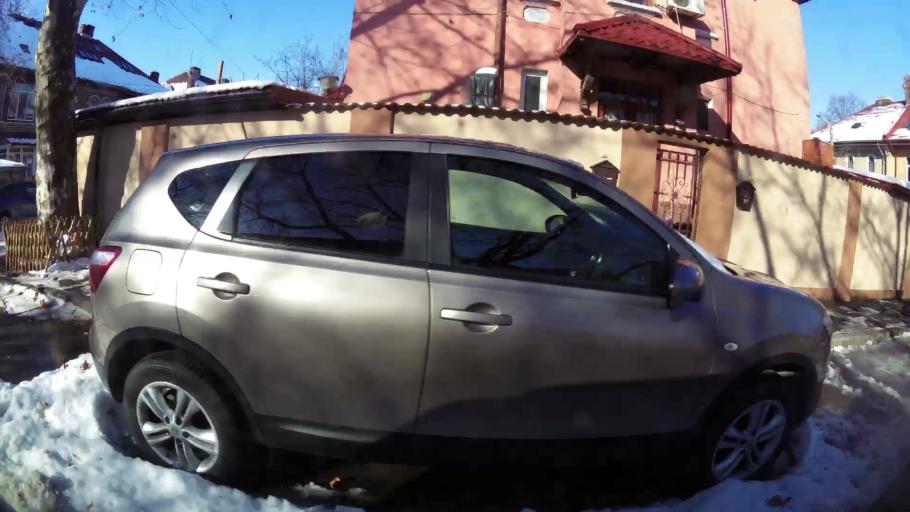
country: RO
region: Bucuresti
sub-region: Municipiul Bucuresti
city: Bucuresti
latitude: 44.4171
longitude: 26.0879
